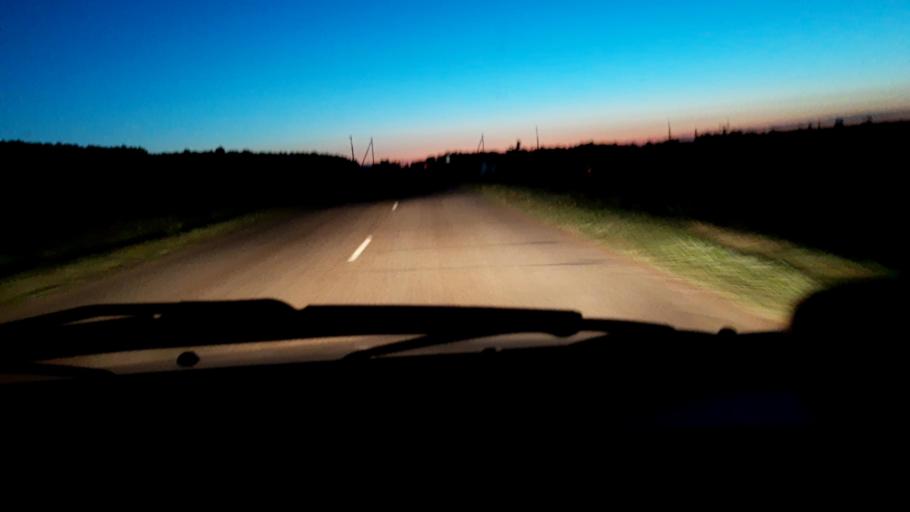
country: RU
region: Bashkortostan
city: Blagoveshchensk
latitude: 54.9343
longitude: 55.8988
